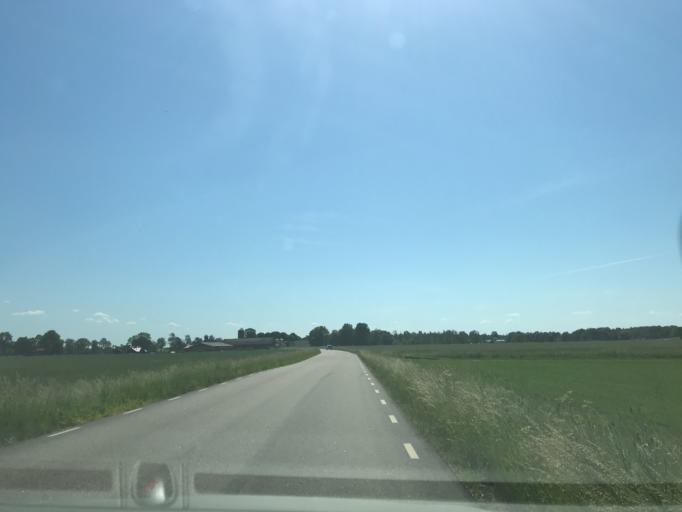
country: SE
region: Vaestra Goetaland
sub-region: Gotene Kommun
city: Kallby
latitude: 58.5195
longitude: 13.3209
